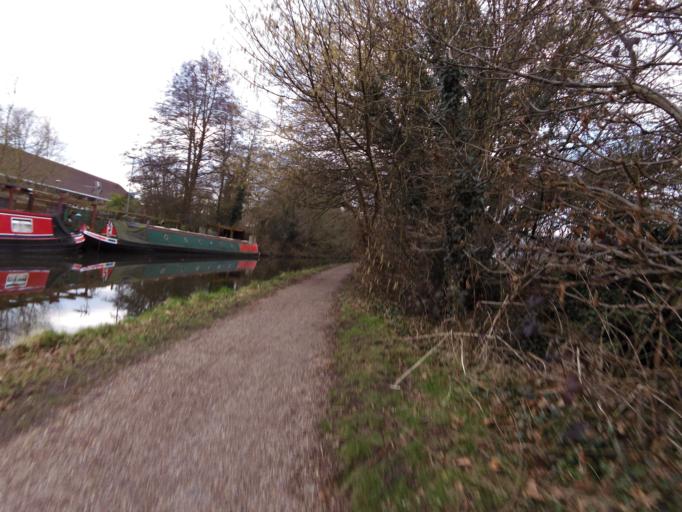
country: GB
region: England
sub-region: Hertfordshire
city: Watford
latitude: 51.6504
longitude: -0.4274
